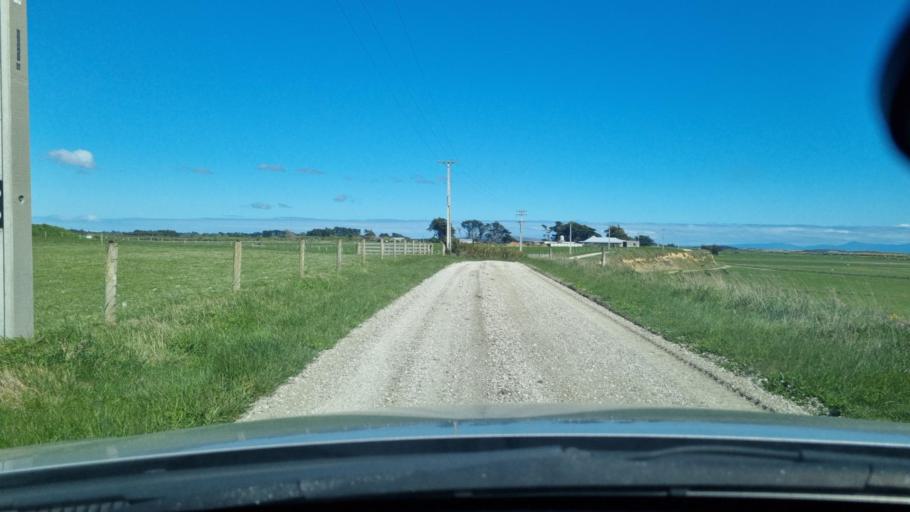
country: NZ
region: Southland
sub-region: Invercargill City
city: Invercargill
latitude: -46.3963
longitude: 168.2577
